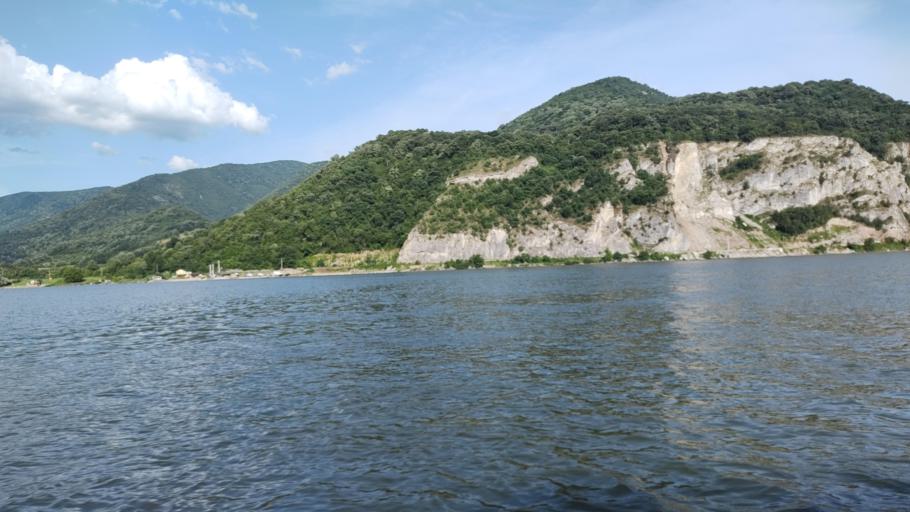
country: RO
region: Caras-Severin
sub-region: Comuna Berzasca
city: Berzasca
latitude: 44.6170
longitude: 22.0011
